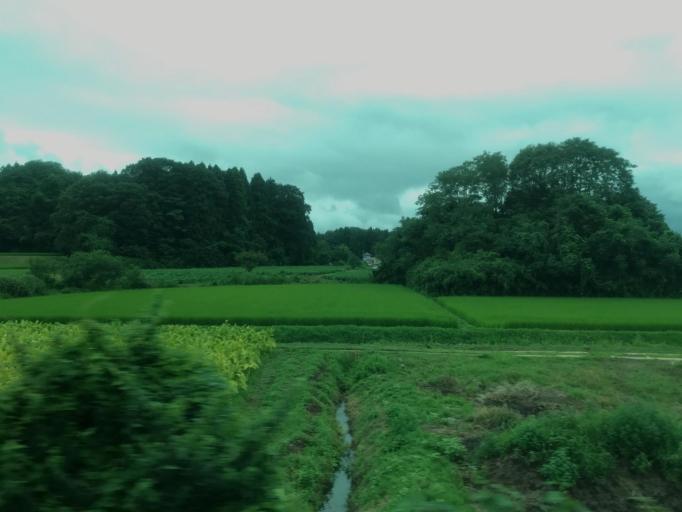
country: JP
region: Fukushima
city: Sukagawa
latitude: 37.1893
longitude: 140.3142
